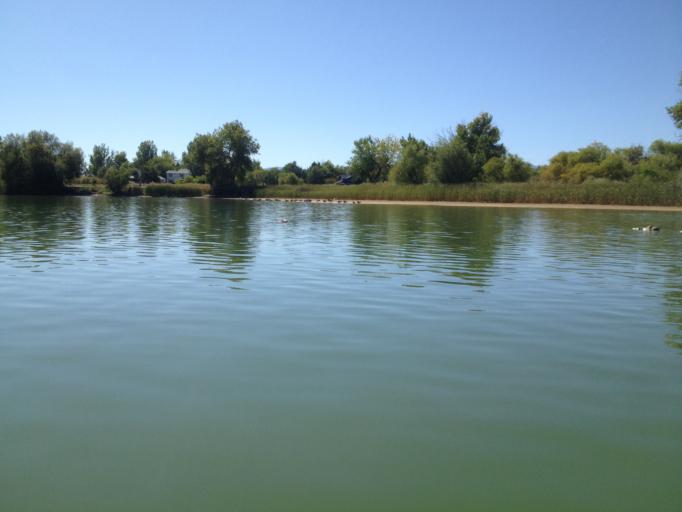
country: US
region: Colorado
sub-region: Boulder County
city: Louisville
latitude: 39.9951
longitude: -105.1146
